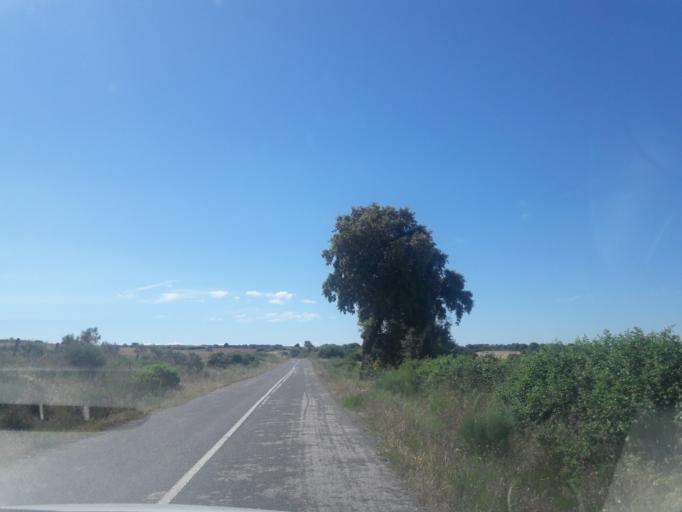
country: ES
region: Castille and Leon
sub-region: Provincia de Salamanca
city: Lumbrales
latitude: 40.9809
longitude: -6.7310
